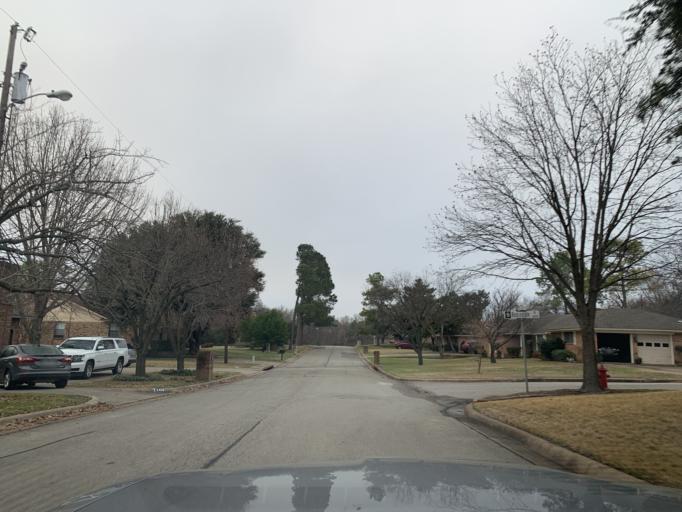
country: US
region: Texas
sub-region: Tarrant County
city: Bedford
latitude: 32.8339
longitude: -97.1523
